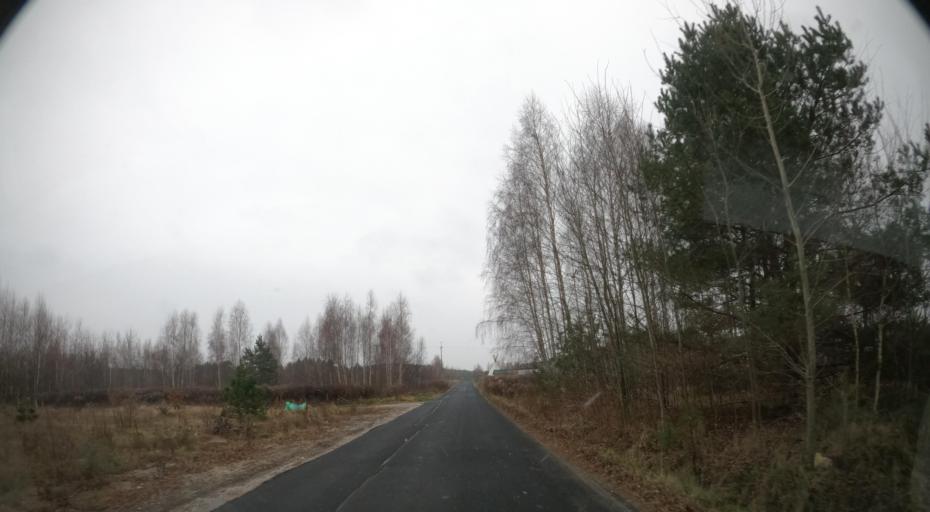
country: PL
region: Masovian Voivodeship
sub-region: Powiat radomski
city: Jedlnia-Letnisko
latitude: 51.4031
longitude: 21.2784
